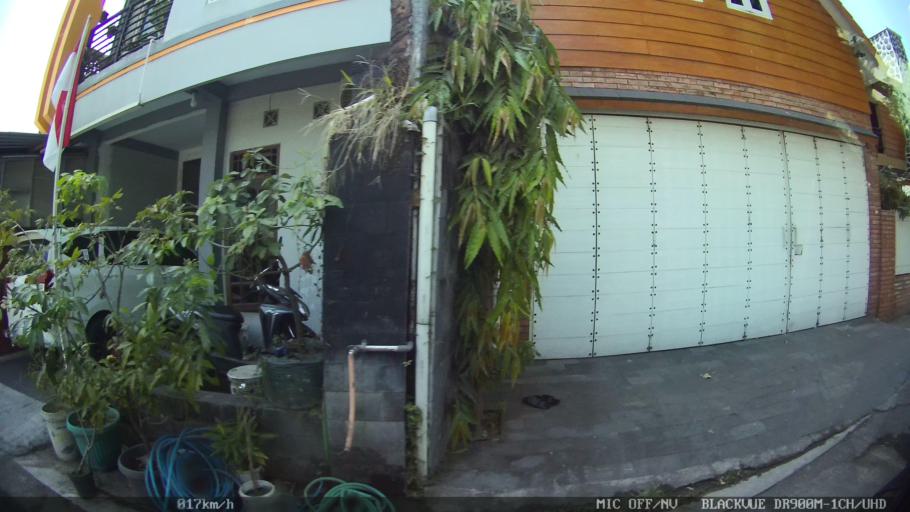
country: ID
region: Daerah Istimewa Yogyakarta
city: Kasihan
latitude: -7.8302
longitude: 110.3779
